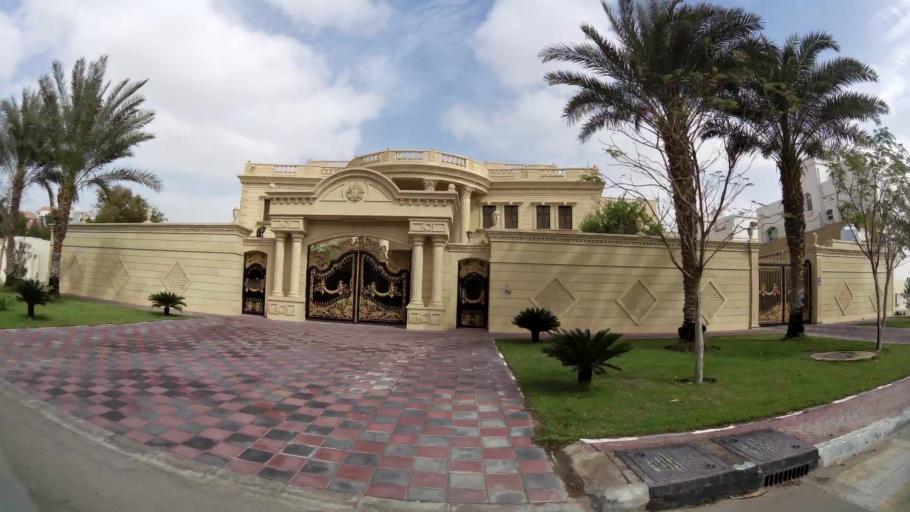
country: AE
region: Abu Dhabi
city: Abu Dhabi
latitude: 24.4034
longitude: 54.5195
